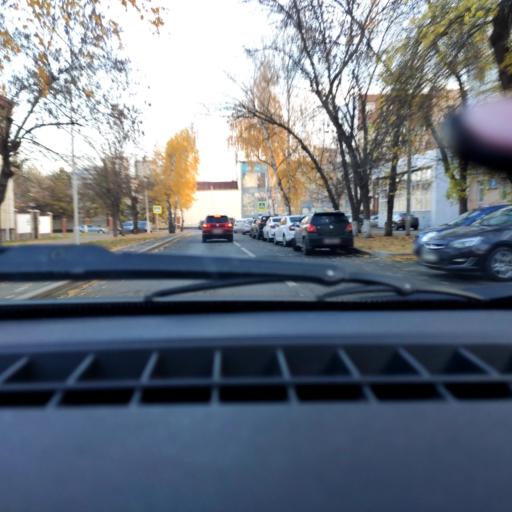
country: RU
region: Bashkortostan
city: Ufa
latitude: 54.7343
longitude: 55.9417
